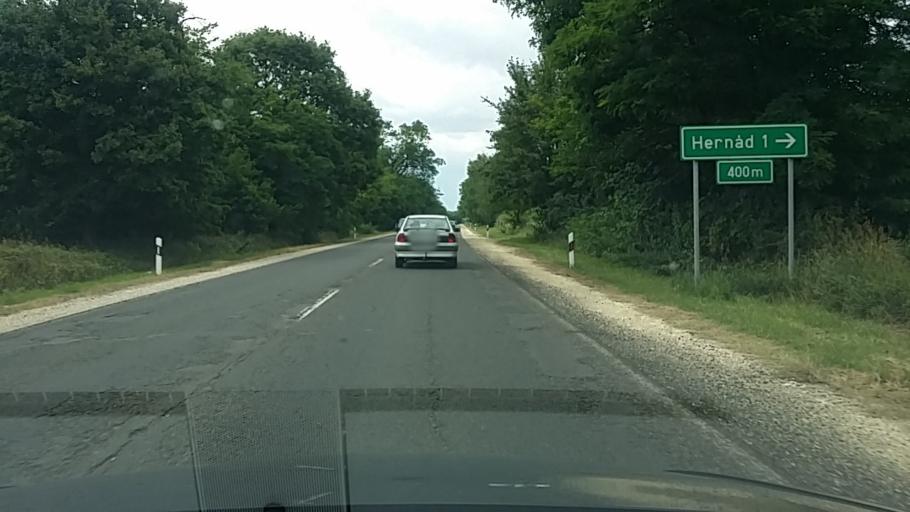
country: HU
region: Pest
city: Hernad
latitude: 47.1484
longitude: 19.3924
